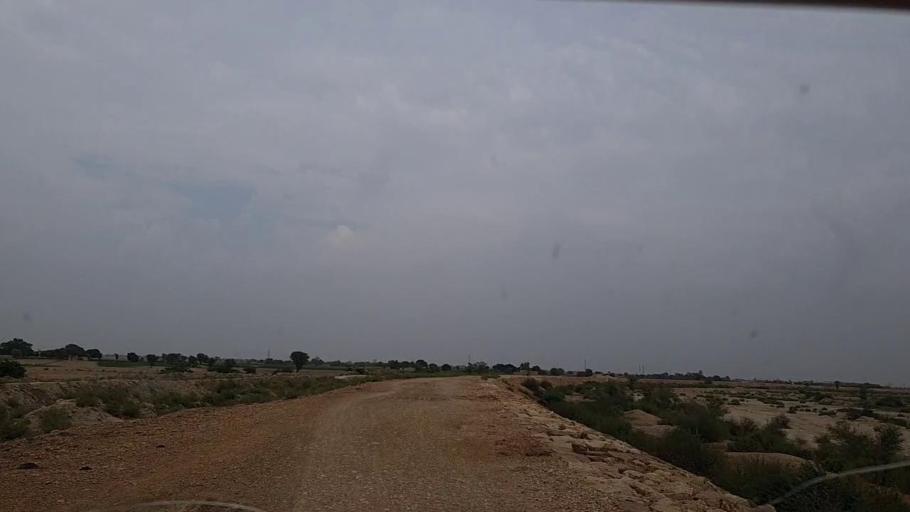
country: PK
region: Sindh
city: Johi
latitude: 26.7042
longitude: 67.5946
